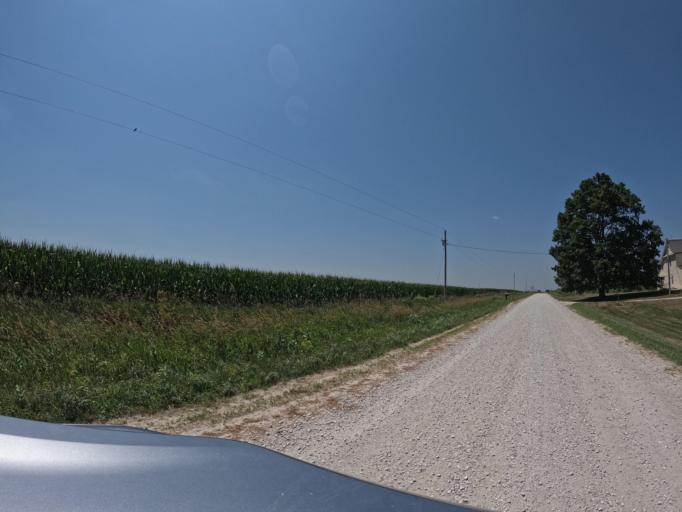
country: US
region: Iowa
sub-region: Keokuk County
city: Sigourney
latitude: 41.2868
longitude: -92.1751
